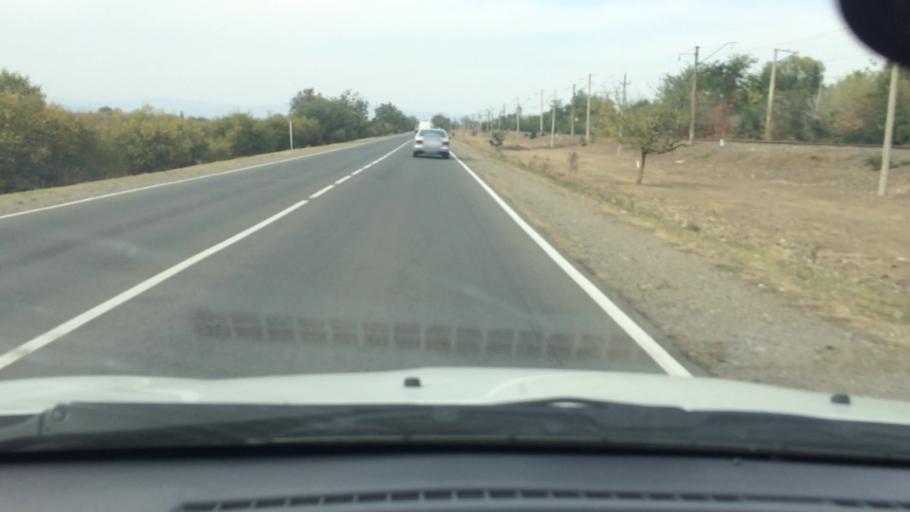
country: GE
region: Kvemo Kartli
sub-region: Marneuli
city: Marneuli
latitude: 41.4244
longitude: 44.8236
